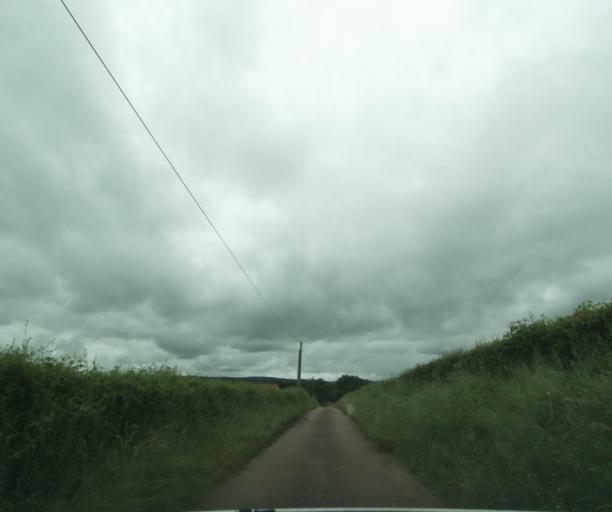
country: FR
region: Bourgogne
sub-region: Departement de Saone-et-Loire
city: Charolles
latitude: 46.4733
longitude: 4.3508
